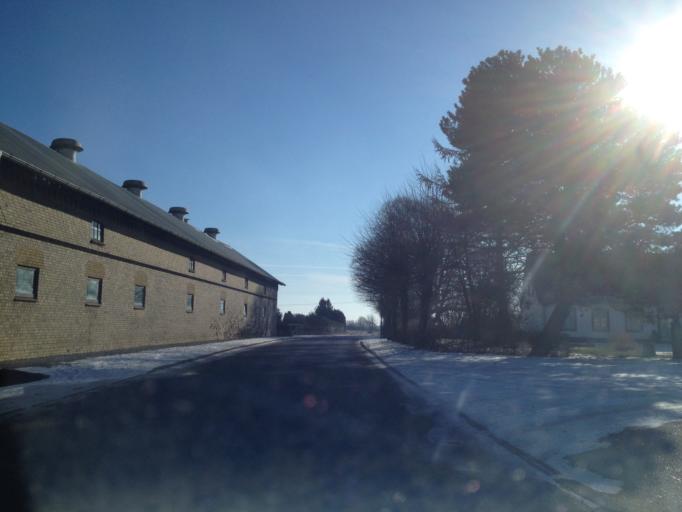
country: DK
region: South Denmark
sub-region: Haderslev Kommune
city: Haderslev
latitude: 55.2876
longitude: 9.4431
